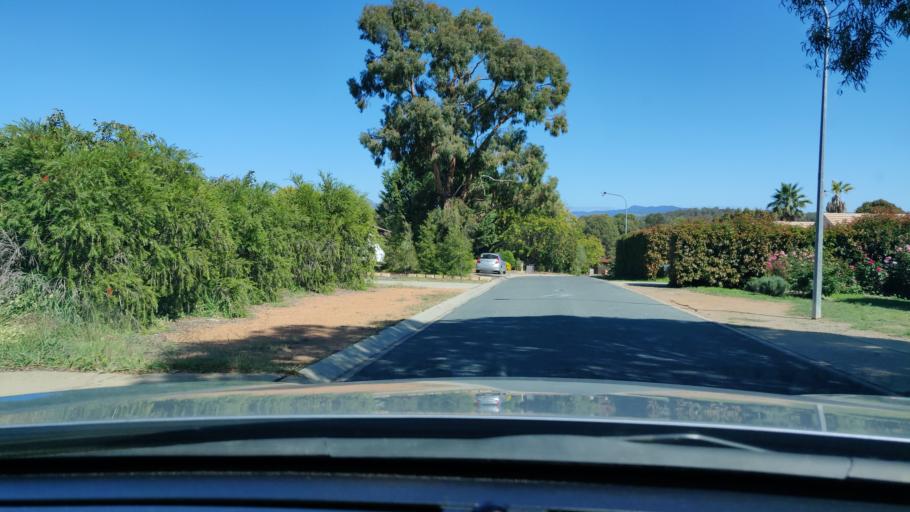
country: AU
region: Australian Capital Territory
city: Macarthur
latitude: -35.4394
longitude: 149.0960
